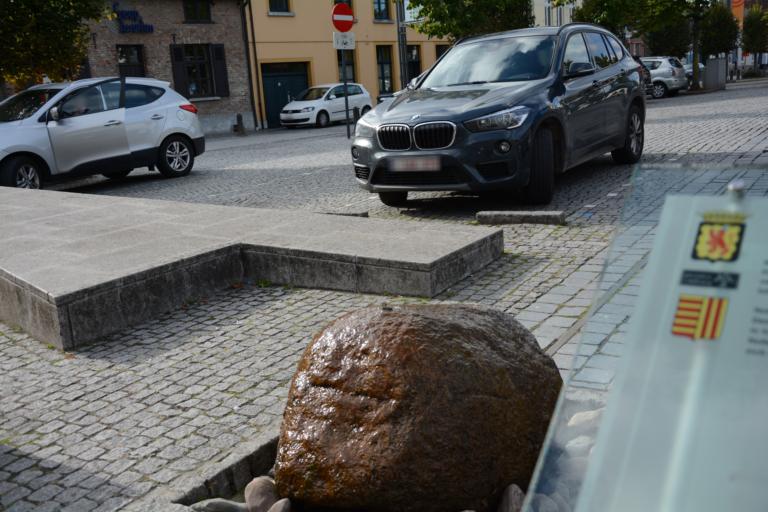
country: BE
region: Flanders
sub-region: Provincie Limburg
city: Peer
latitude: 51.1318
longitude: 5.4549
